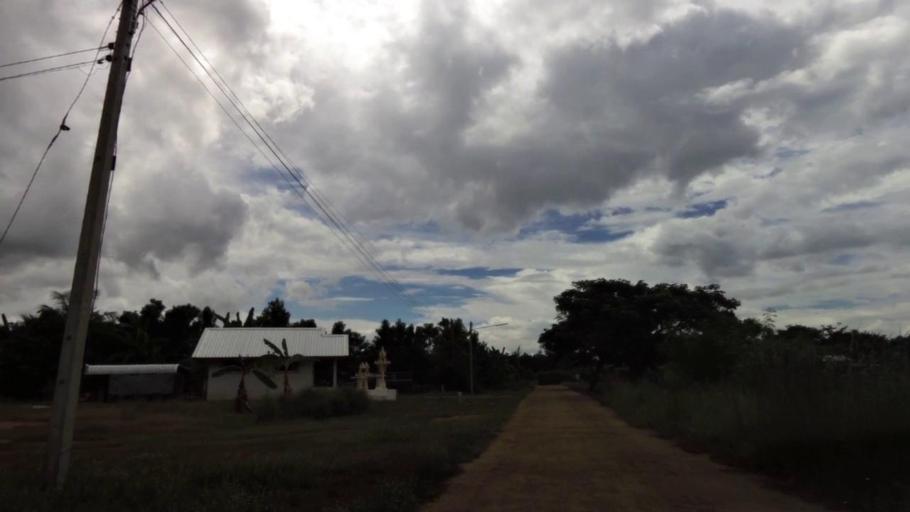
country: TH
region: Nakhon Sawan
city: Phai Sali
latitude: 15.6072
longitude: 100.6556
